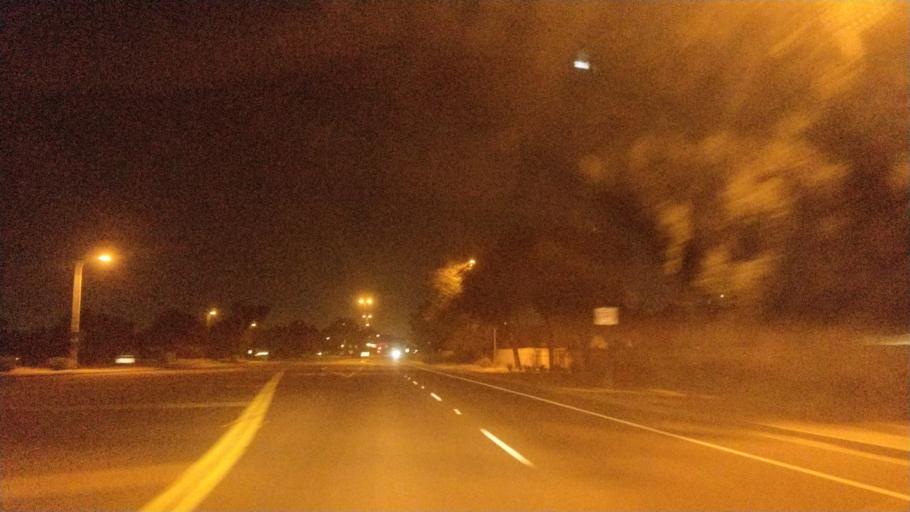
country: US
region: Arizona
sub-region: Maricopa County
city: Sun Lakes
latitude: 33.2525
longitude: -111.8840
